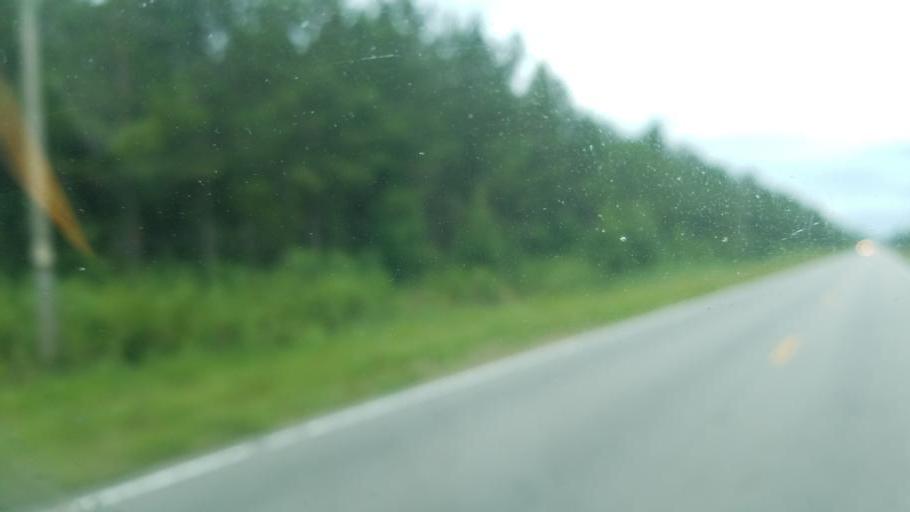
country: US
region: North Carolina
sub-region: Tyrrell County
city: Columbia
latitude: 35.9335
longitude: -76.1662
